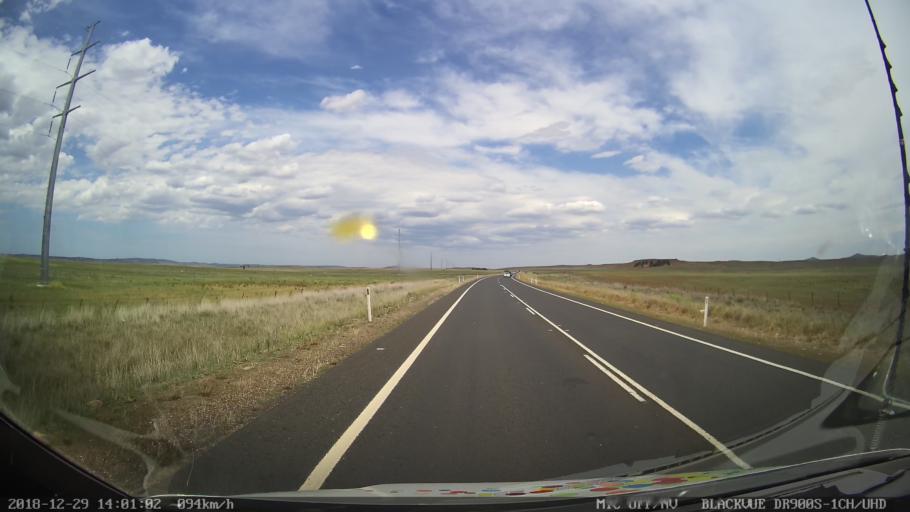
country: AU
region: New South Wales
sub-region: Cooma-Monaro
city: Cooma
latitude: -36.2701
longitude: 149.1655
